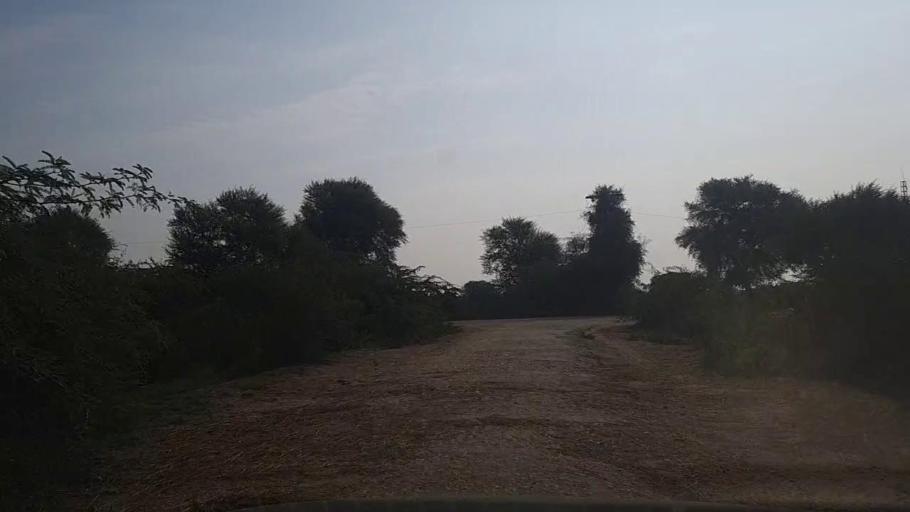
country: PK
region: Sindh
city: Bulri
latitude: 24.9695
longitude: 68.3307
